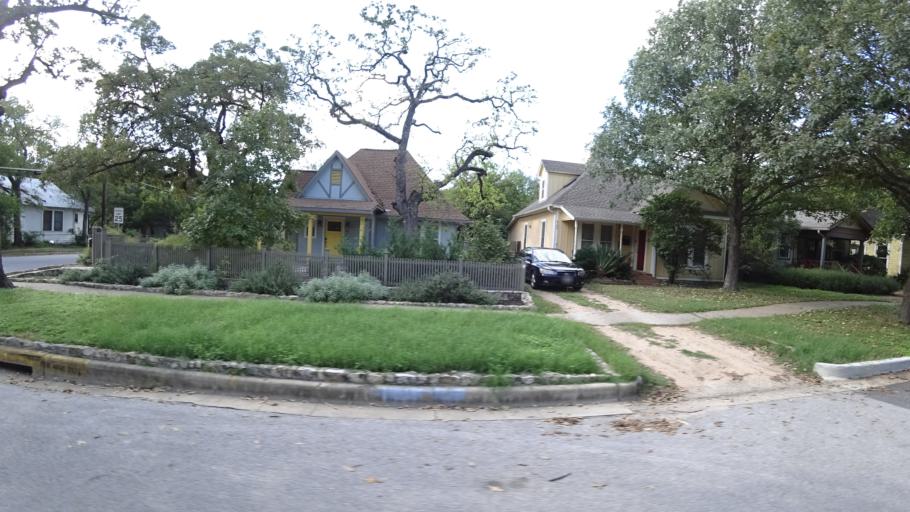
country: US
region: Texas
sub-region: Travis County
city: Austin
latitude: 30.3057
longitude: -97.7338
